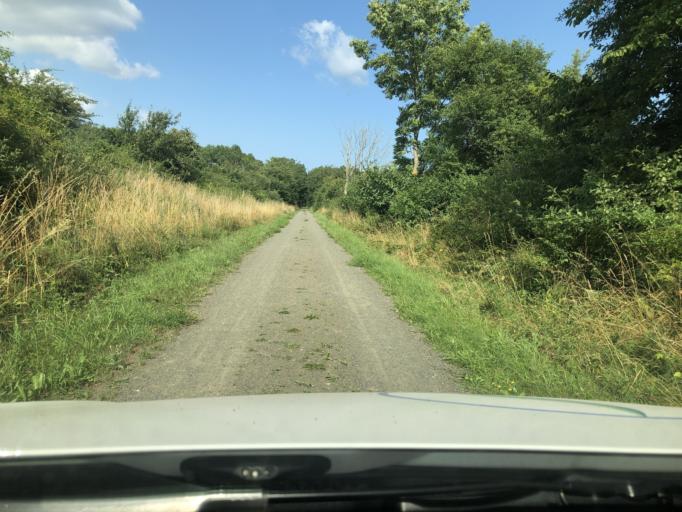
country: SE
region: Skane
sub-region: Kristianstads Kommun
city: Degeberga
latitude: 55.7730
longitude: 14.1604
